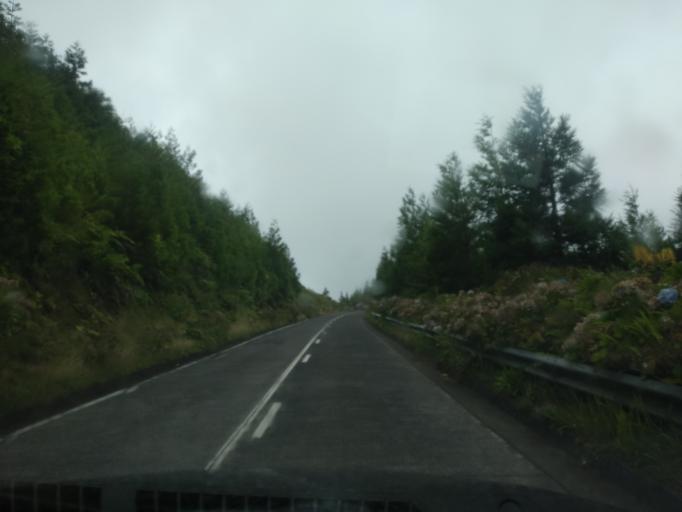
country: PT
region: Azores
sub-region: Ponta Delgada
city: Arrifes
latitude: 37.8371
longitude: -25.7833
